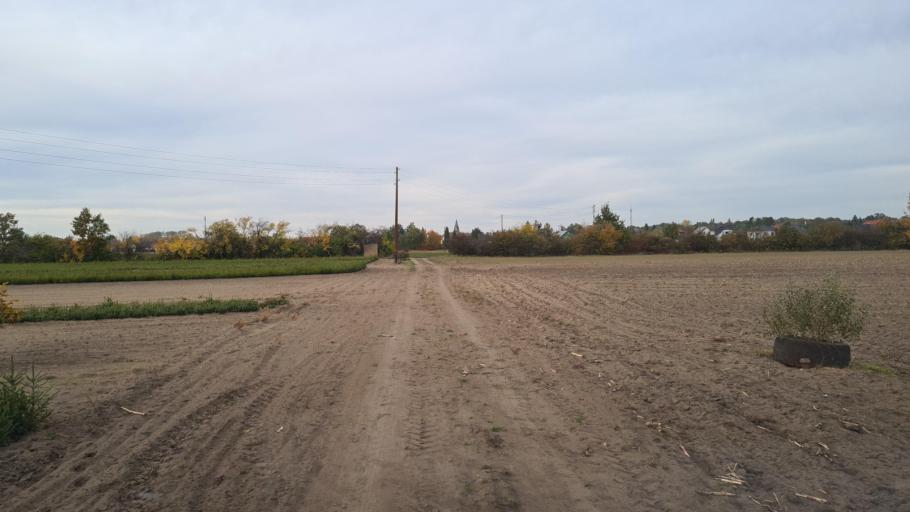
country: DE
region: Brandenburg
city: Bad Liebenwerda
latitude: 51.5051
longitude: 13.4014
